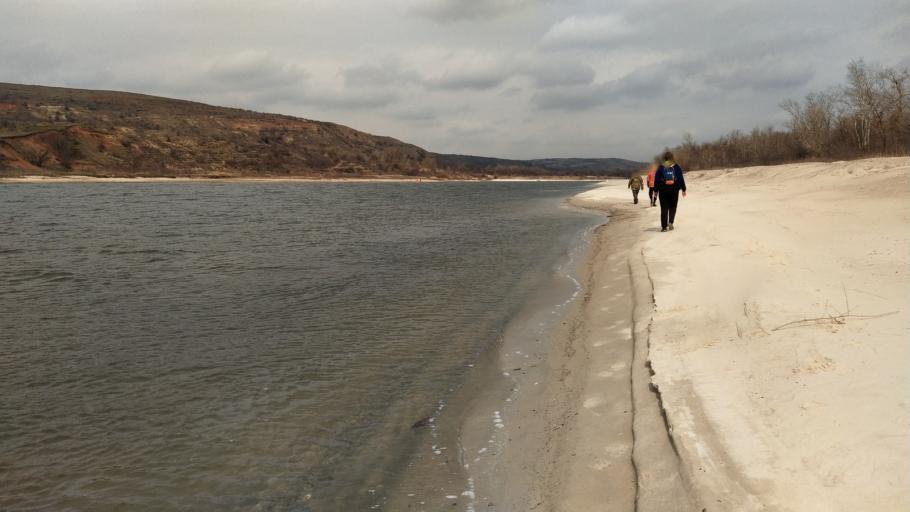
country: RU
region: Rostov
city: Semikarakorsk
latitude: 47.5563
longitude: 40.6727
